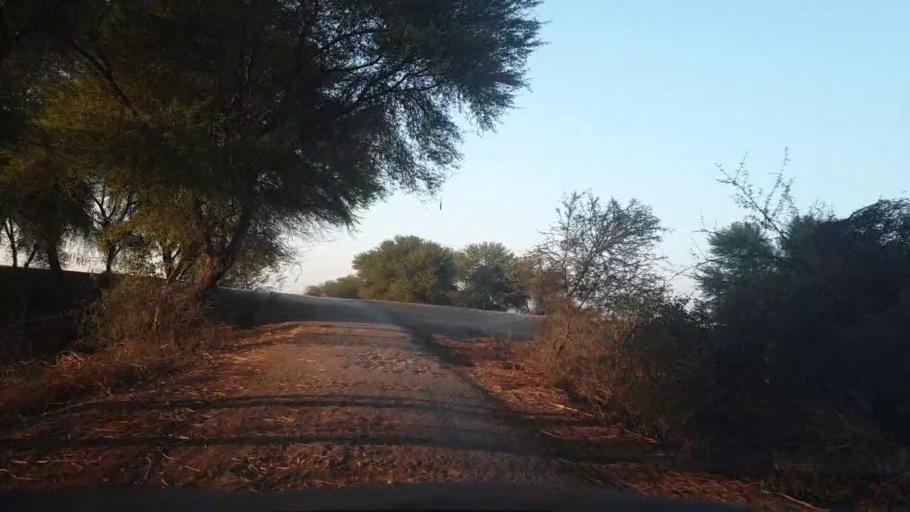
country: PK
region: Sindh
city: Ubauro
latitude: 28.1880
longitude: 69.6012
